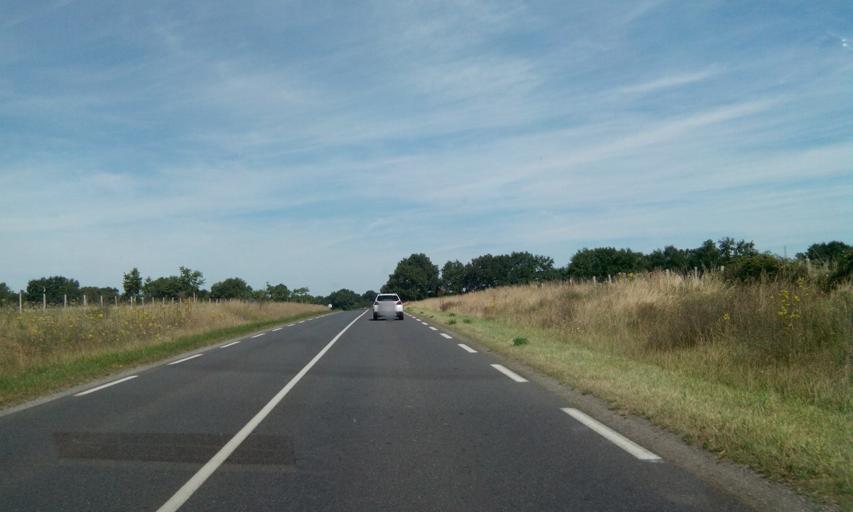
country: FR
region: Poitou-Charentes
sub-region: Departement de la Vienne
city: Charroux
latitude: 46.1447
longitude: 0.4165
